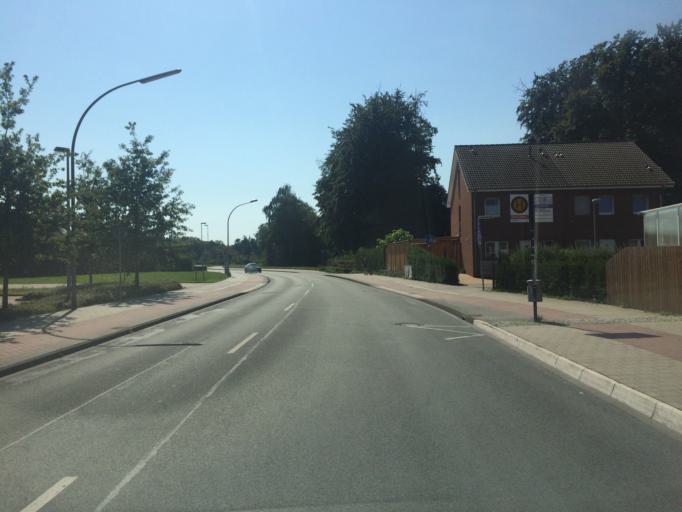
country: DE
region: North Rhine-Westphalia
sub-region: Regierungsbezirk Munster
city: Telgte
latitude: 51.9962
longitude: 7.7108
